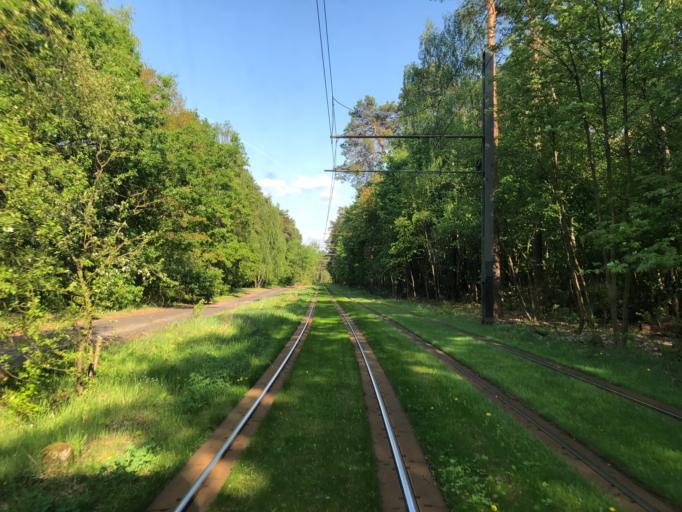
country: DE
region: Berlin
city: Grunau
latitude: 52.4066
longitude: 13.6132
